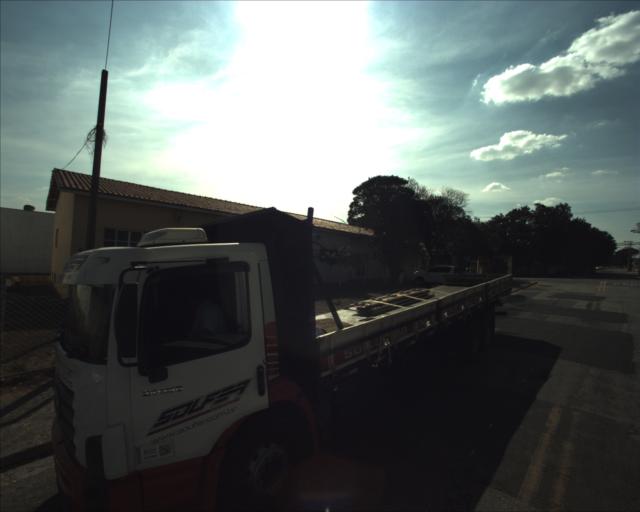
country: BR
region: Sao Paulo
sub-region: Sorocaba
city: Sorocaba
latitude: -23.4728
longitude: -47.4393
